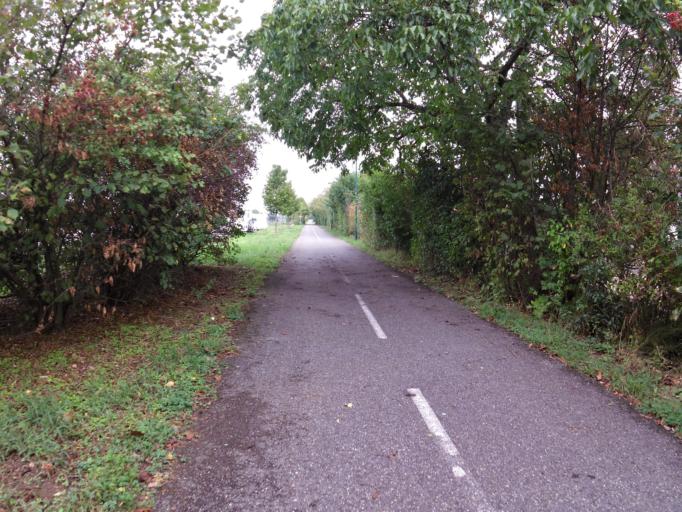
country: FR
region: Alsace
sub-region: Departement du Haut-Rhin
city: Fessenheim
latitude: 47.9185
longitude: 7.5321
